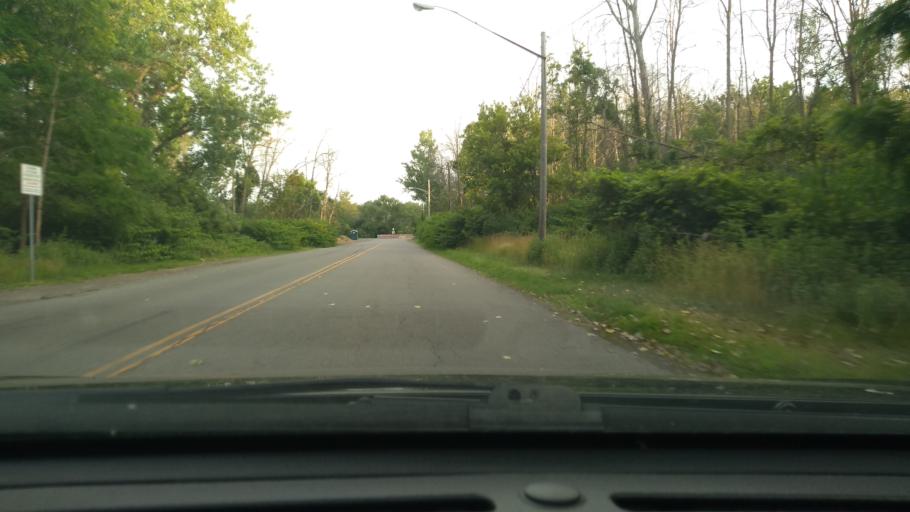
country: US
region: New York
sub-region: Erie County
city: Lackawanna
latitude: 42.8334
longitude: -78.8325
